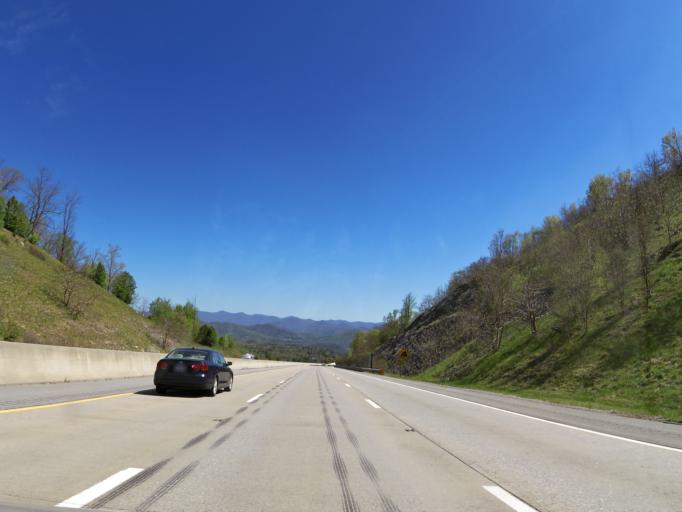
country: US
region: North Carolina
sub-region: Madison County
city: Mars Hill
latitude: 35.8698
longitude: -82.5376
